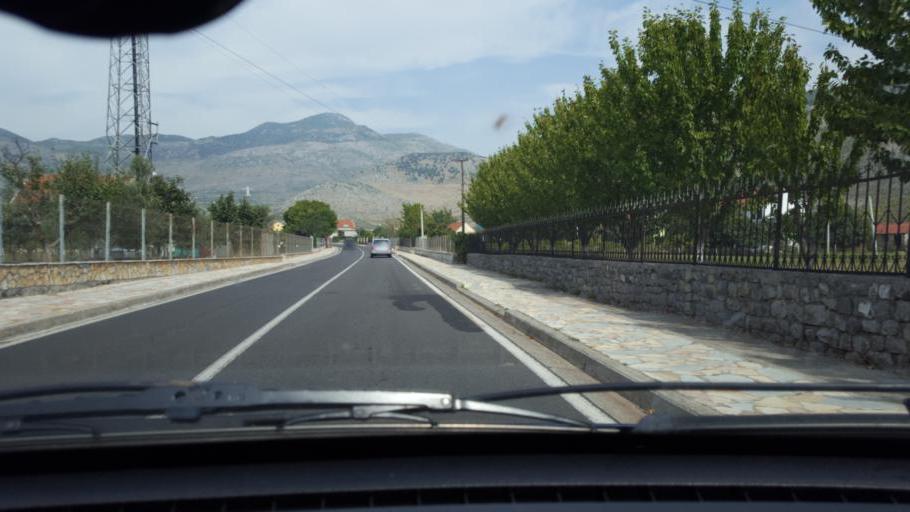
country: AL
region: Shkoder
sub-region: Rrethi i Malesia e Madhe
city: Hot
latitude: 42.3419
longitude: 19.4382
